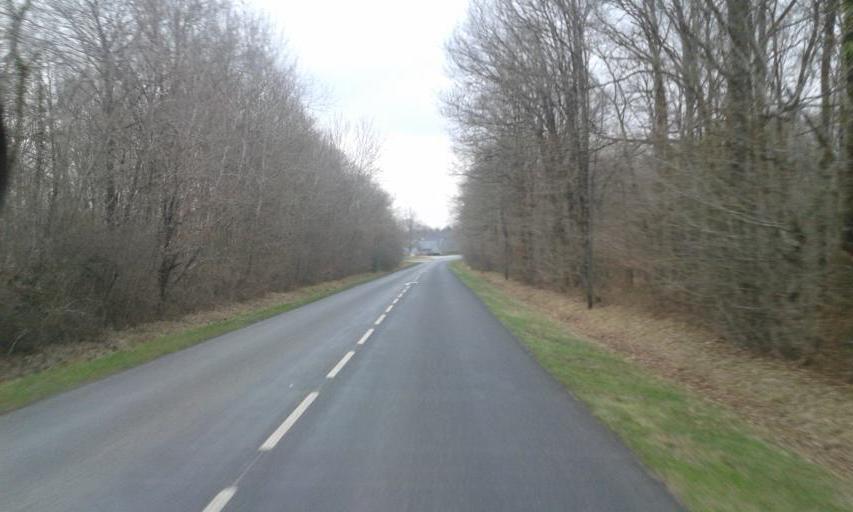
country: FR
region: Centre
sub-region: Departement du Loir-et-Cher
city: Dhuizon
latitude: 47.6457
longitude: 1.6674
